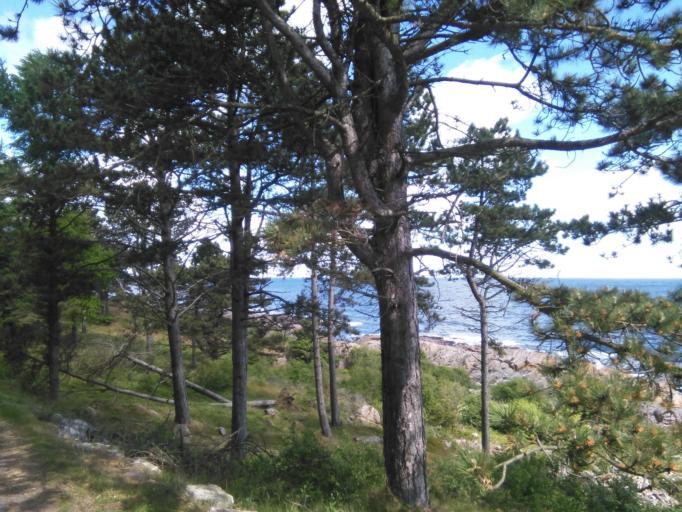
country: DK
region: Capital Region
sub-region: Bornholm Kommune
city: Ronne
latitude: 55.2965
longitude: 14.7763
